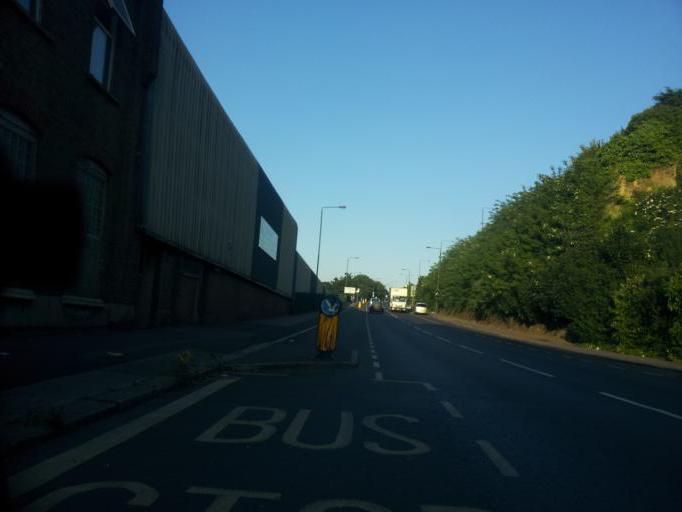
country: GB
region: England
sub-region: Greater London
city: Erith
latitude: 51.4811
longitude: 0.1720
